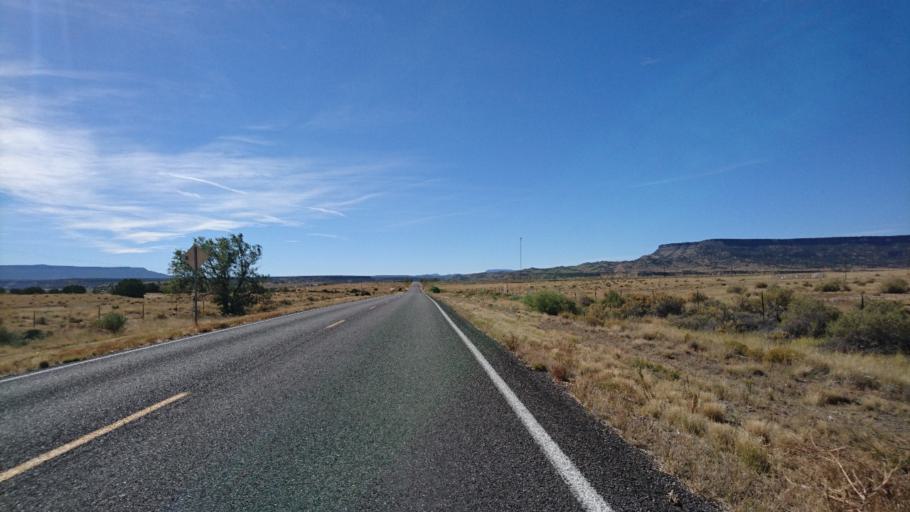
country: US
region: New Mexico
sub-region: Cibola County
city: Skyline-Ganipa
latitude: 35.0815
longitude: -107.6323
